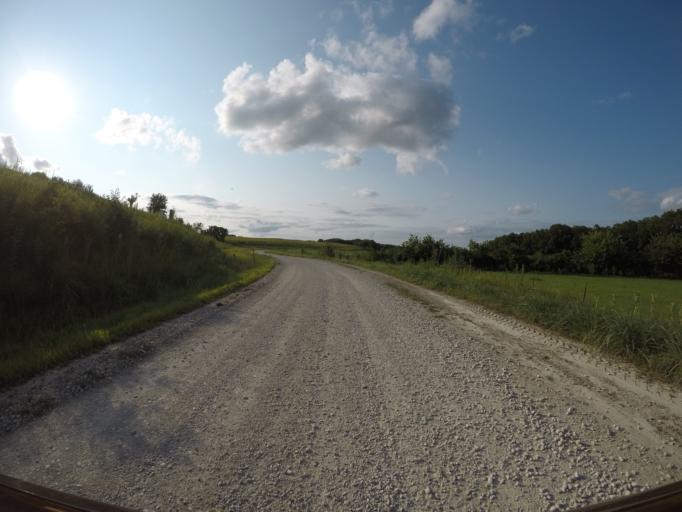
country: US
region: Kansas
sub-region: Wabaunsee County
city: Alma
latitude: 38.8803
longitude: -96.2061
